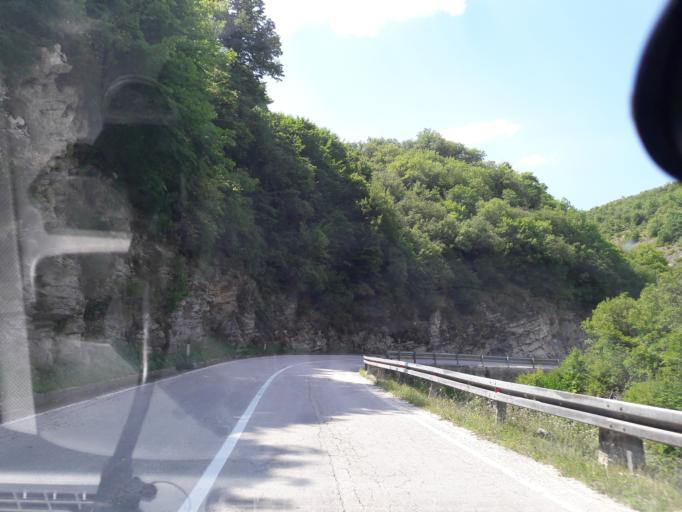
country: BA
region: Republika Srpska
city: Mrkonjic Grad
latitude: 44.4564
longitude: 17.1607
